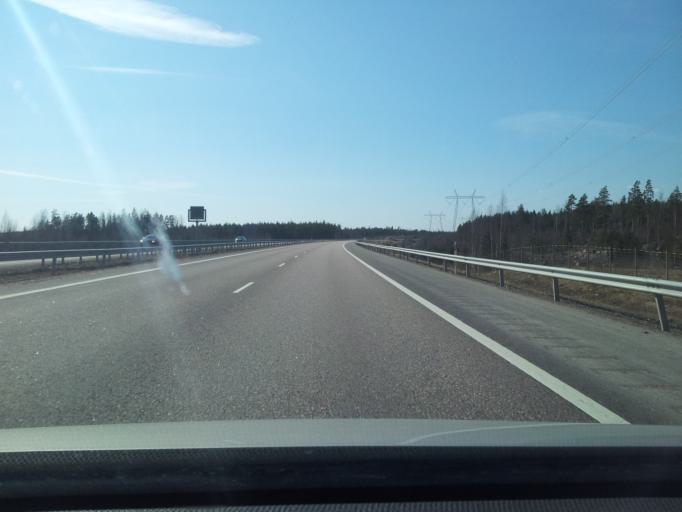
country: FI
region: Uusimaa
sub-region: Loviisa
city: Ruotsinpyhtaeae
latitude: 60.4889
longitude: 26.4014
